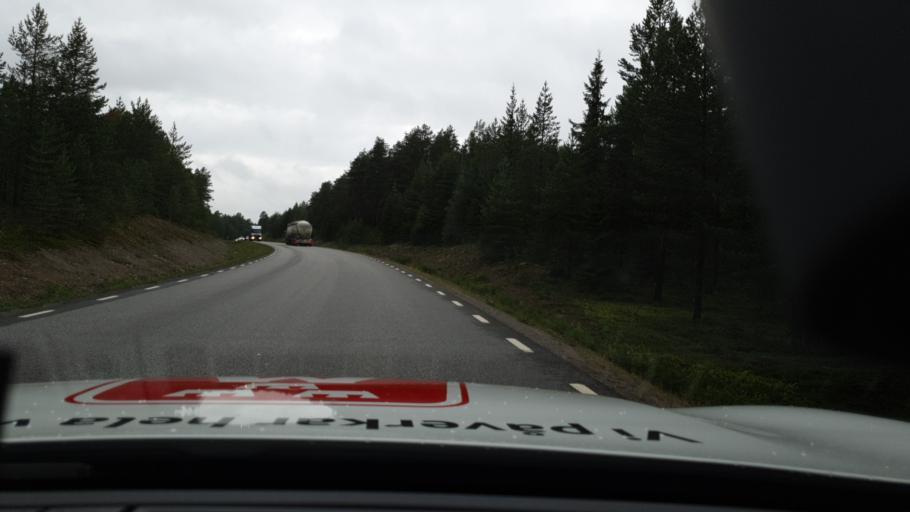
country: SE
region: Norrbotten
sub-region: Lulea Kommun
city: Ranea
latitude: 65.8601
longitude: 22.3211
